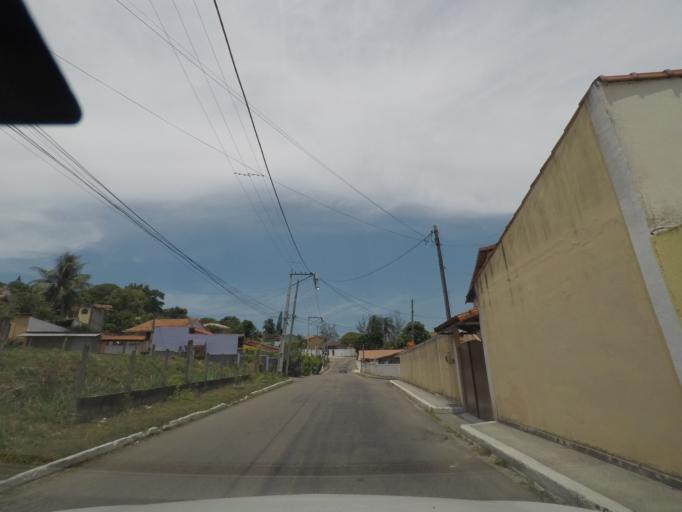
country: BR
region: Rio de Janeiro
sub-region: Marica
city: Marica
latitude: -22.9245
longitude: -42.8171
